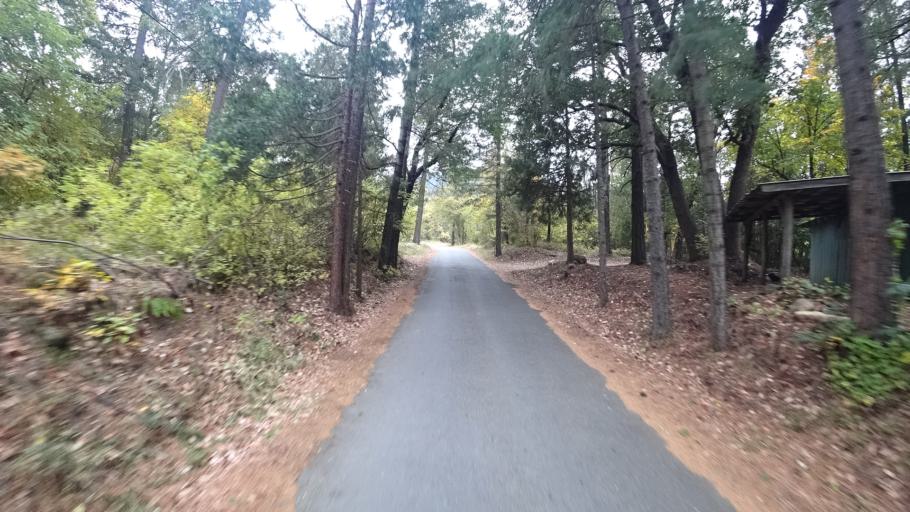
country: US
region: California
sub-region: Siskiyou County
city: Happy Camp
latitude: 41.8339
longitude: -123.1730
